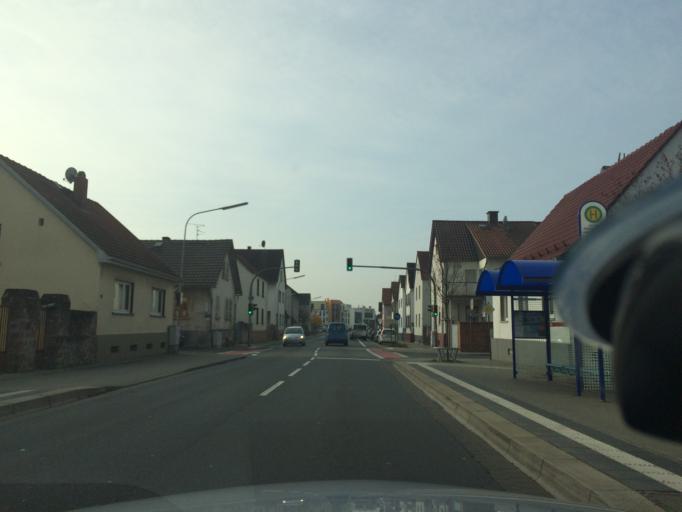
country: DE
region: Hesse
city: Morfelden-Walldorf
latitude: 49.9714
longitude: 8.5691
